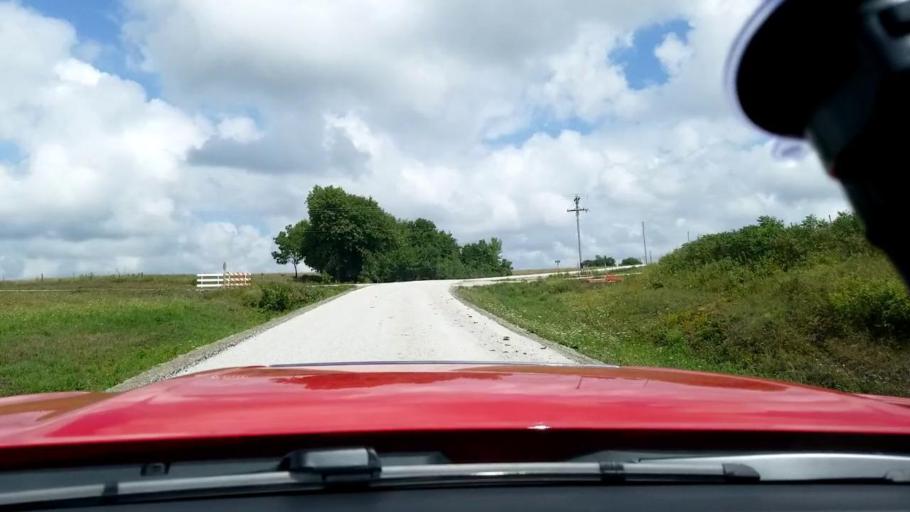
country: US
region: Iowa
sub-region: Decatur County
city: Lamoni
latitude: 40.6523
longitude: -94.0530
